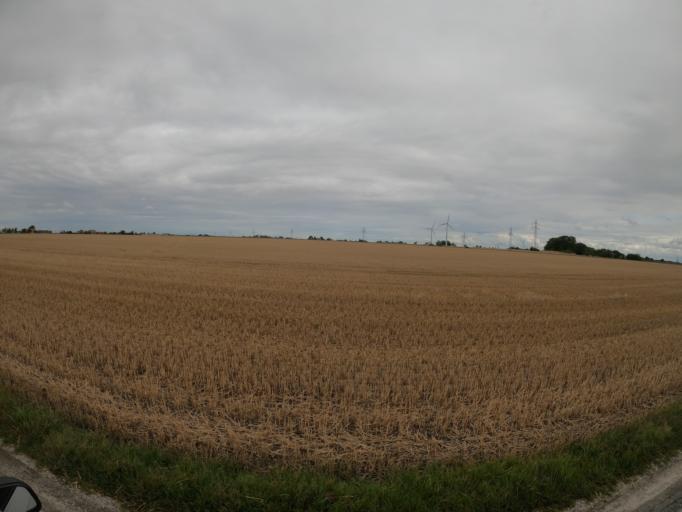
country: SE
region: Skane
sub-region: Kavlinge Kommun
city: Kaevlinge
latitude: 55.7458
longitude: 13.1386
